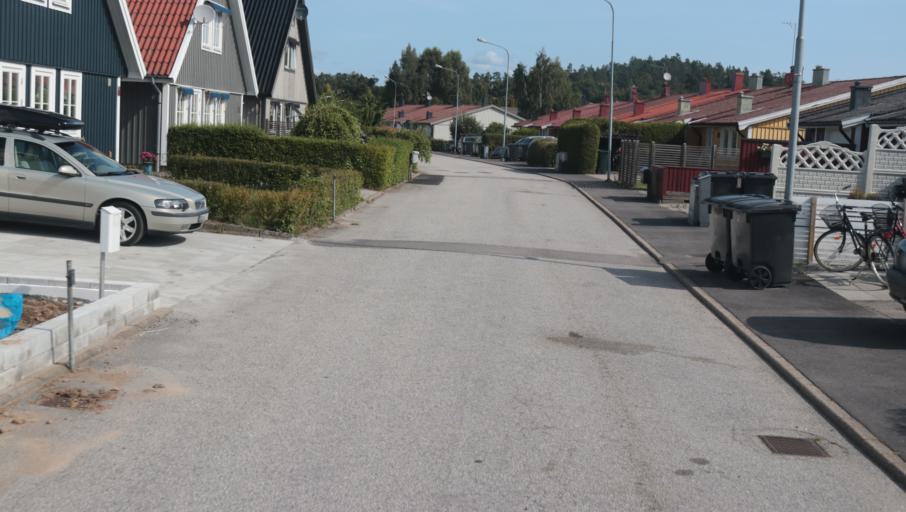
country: SE
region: Blekinge
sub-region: Karlshamns Kommun
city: Karlshamn
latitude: 56.1967
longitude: 14.8487
